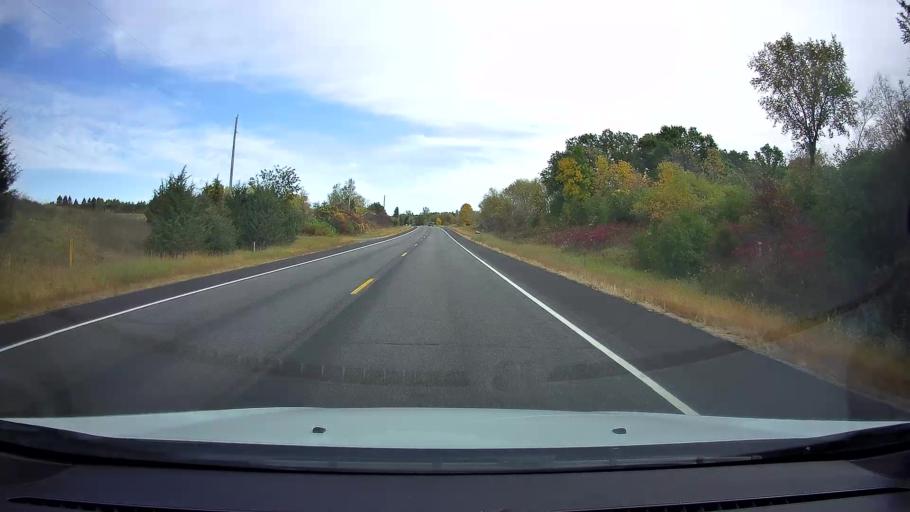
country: US
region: Minnesota
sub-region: Washington County
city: Stillwater
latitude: 45.1234
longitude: -92.7665
